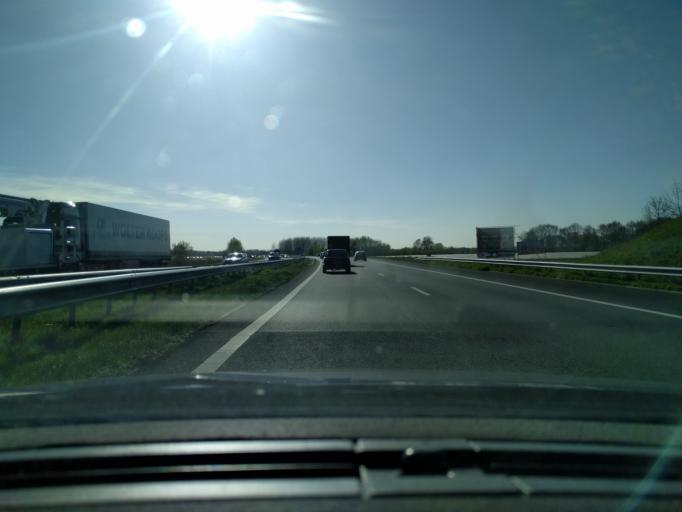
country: NL
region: North Brabant
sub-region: Gemeente Veghel
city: Veghel
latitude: 51.6324
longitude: 5.5238
